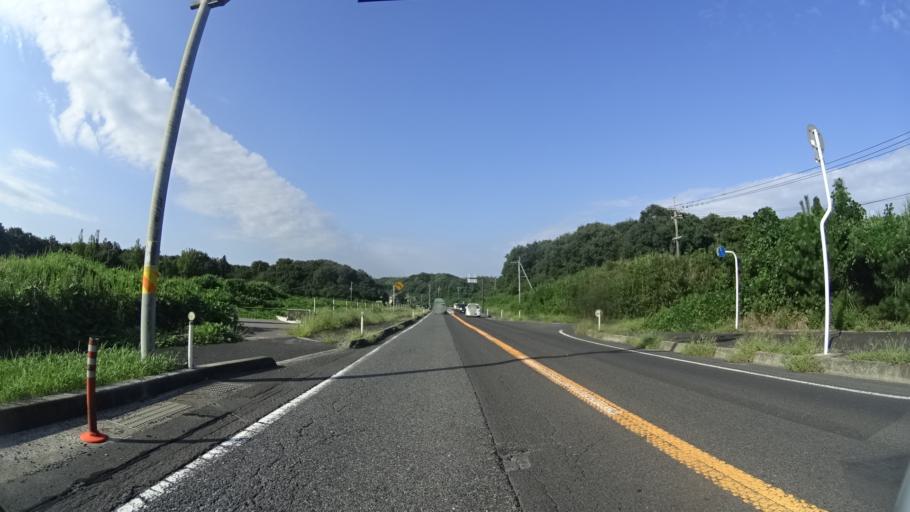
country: JP
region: Shimane
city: Izumo
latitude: 35.3027
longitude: 132.6516
